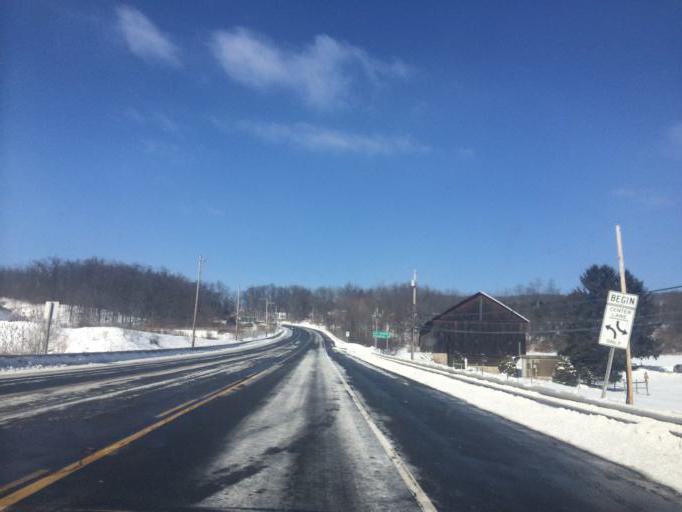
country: US
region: Pennsylvania
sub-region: Centre County
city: Park Forest Village
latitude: 40.8235
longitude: -77.9452
